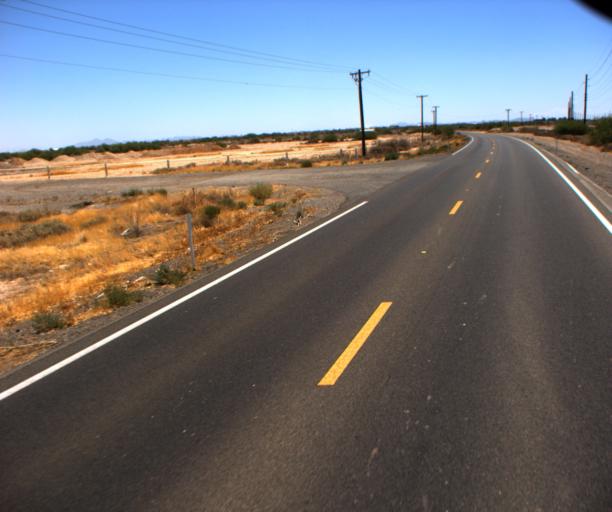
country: US
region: Arizona
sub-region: Pinal County
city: Maricopa
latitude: 33.0733
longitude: -112.0813
